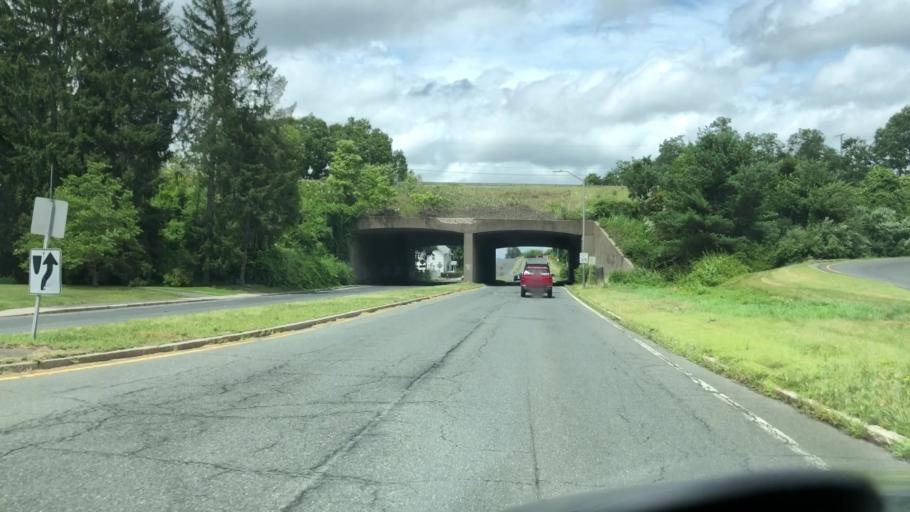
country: US
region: Massachusetts
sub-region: Hampden County
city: Chicopee
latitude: 42.1560
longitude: -72.6114
